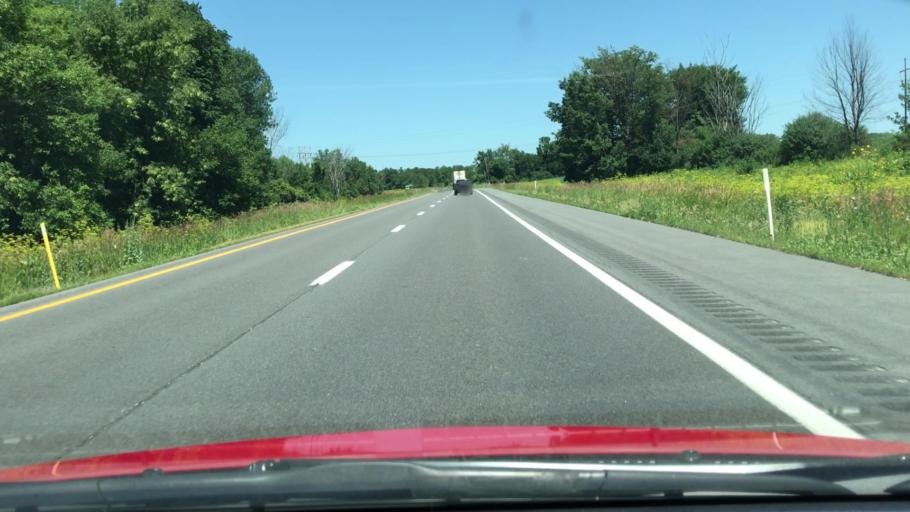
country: US
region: New York
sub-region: Clinton County
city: Cumberland Head
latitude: 44.7407
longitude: -73.4306
